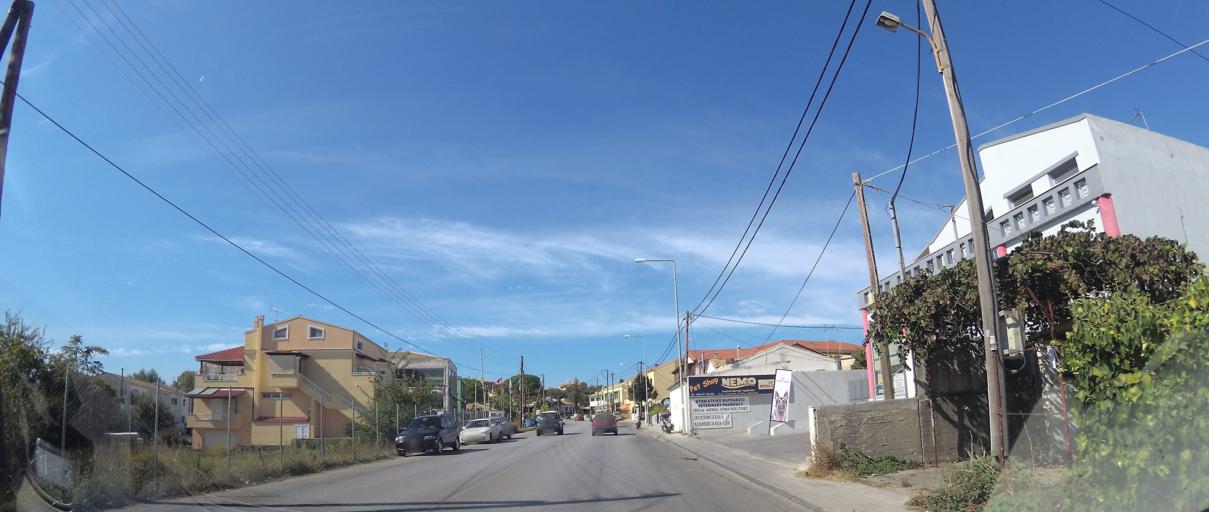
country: GR
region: Ionian Islands
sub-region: Nomos Kerkyras
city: Alepou
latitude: 39.6163
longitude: 19.9004
